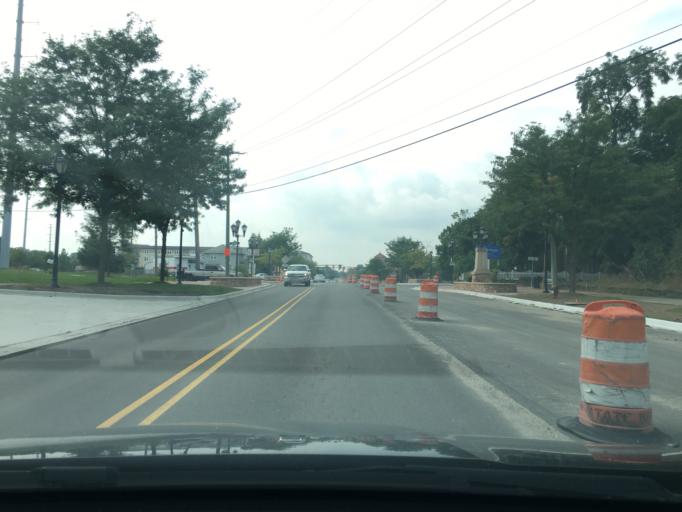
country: US
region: Michigan
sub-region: Oakland County
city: Auburn Hills
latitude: 42.6338
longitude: -83.2174
